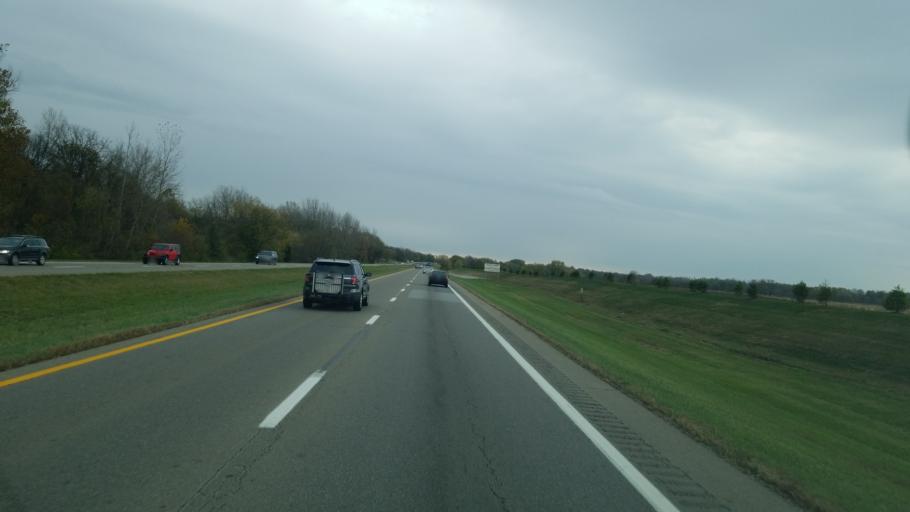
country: US
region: Ohio
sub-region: Pickaway County
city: Commercial Point
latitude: 39.7962
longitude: -82.9914
